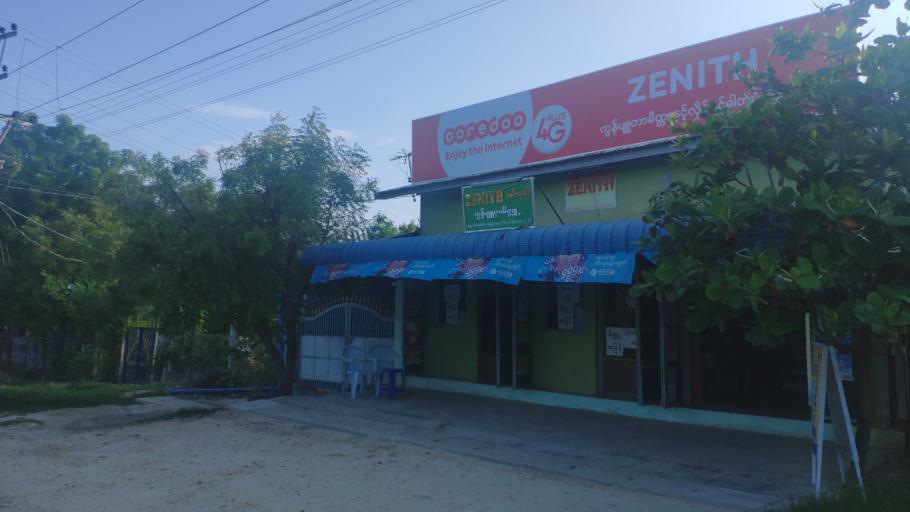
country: MM
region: Mandalay
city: Meiktila
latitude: 20.9046
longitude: 95.8632
